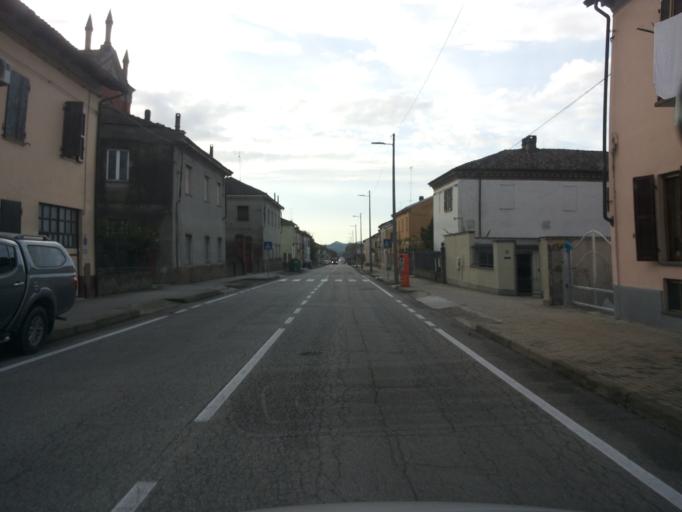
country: IT
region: Piedmont
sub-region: Provincia di Alessandria
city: Ozzano Monferrato
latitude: 45.1073
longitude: 8.3672
